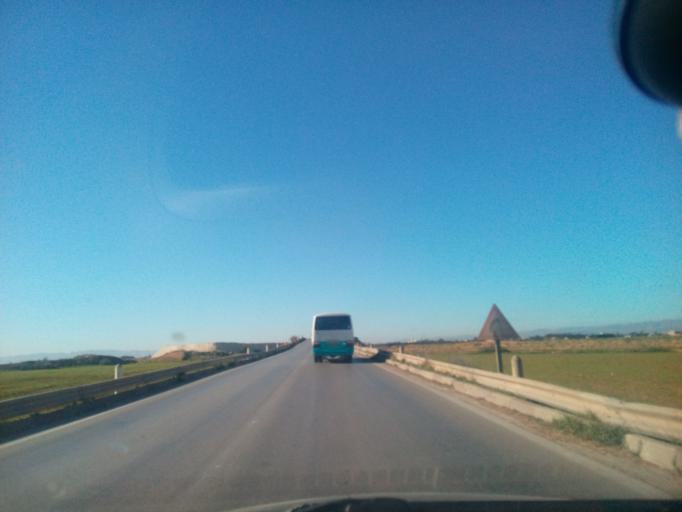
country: DZ
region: Relizane
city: Djidiouia
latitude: 35.8956
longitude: 0.7157
